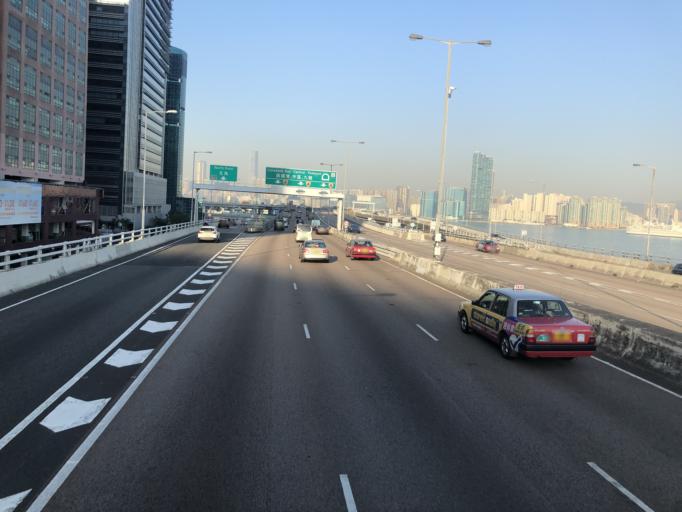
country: HK
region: Kowloon City
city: Kowloon
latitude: 22.2930
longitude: 114.2079
